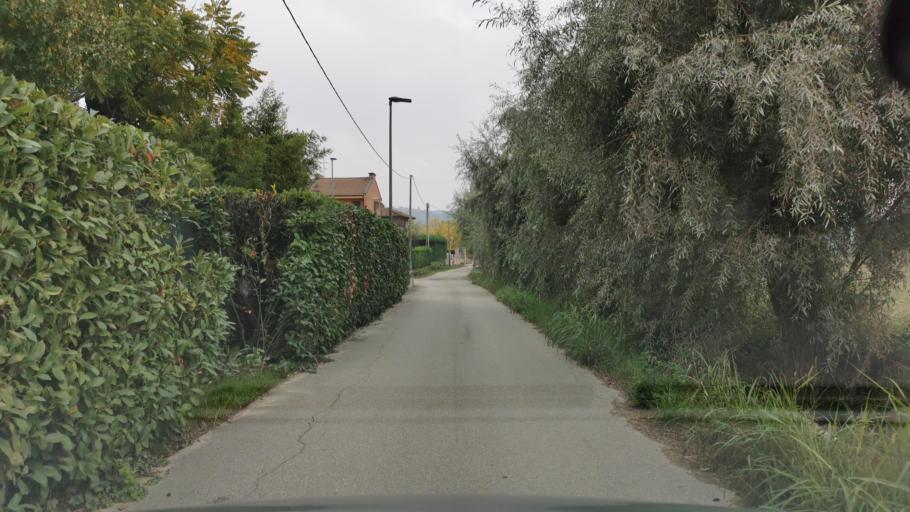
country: IT
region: Piedmont
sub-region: Provincia di Cuneo
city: Cinzano
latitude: 44.6930
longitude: 7.9118
